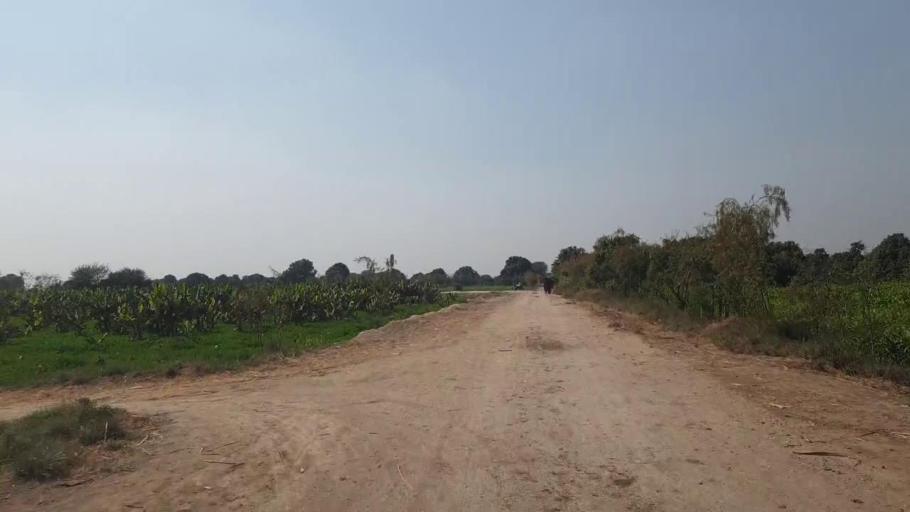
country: PK
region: Sindh
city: Chambar
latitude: 25.3768
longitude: 68.8769
